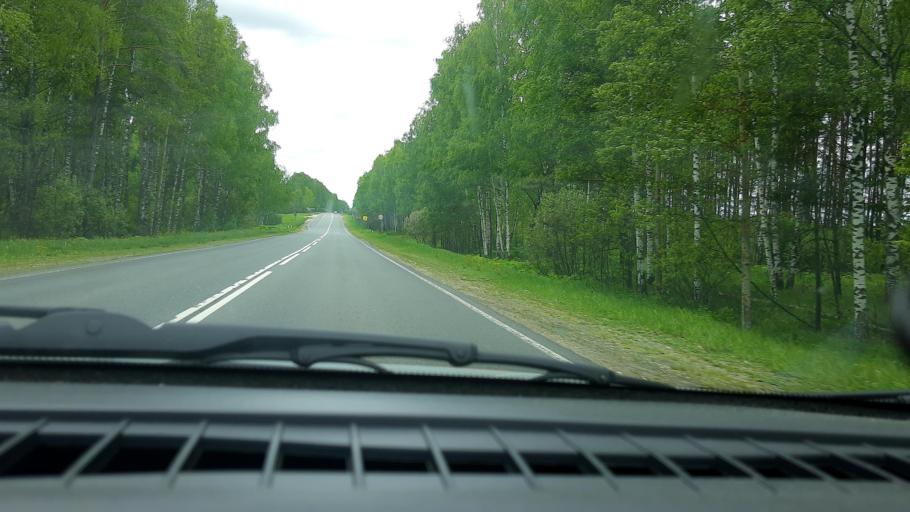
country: RU
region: Nizjnij Novgorod
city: Sukhobezvodnoye
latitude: 56.8610
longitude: 44.8897
